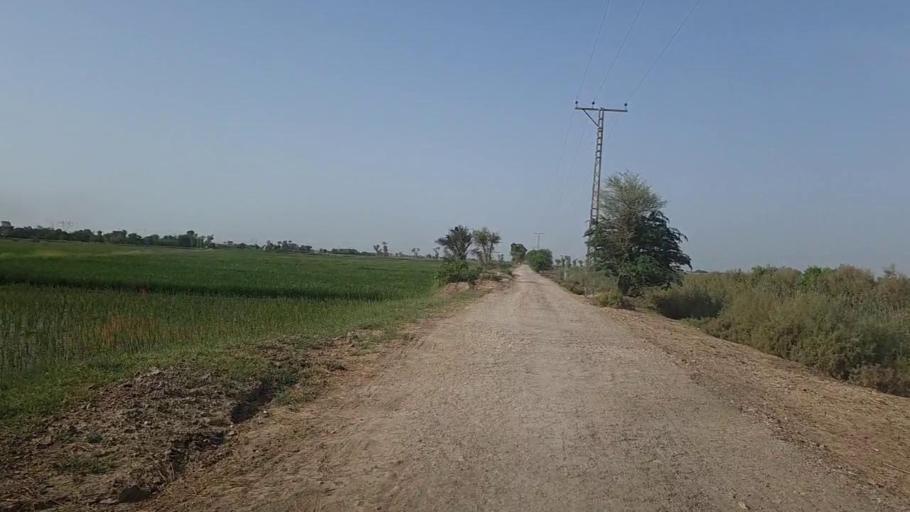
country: PK
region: Sindh
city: Sita Road
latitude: 27.1052
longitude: 67.8745
